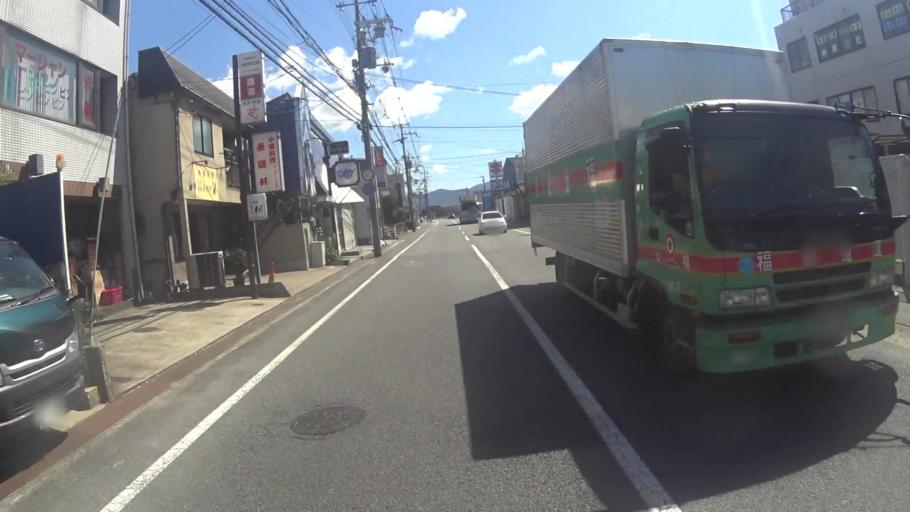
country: JP
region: Kyoto
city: Uji
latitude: 34.8885
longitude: 135.7541
